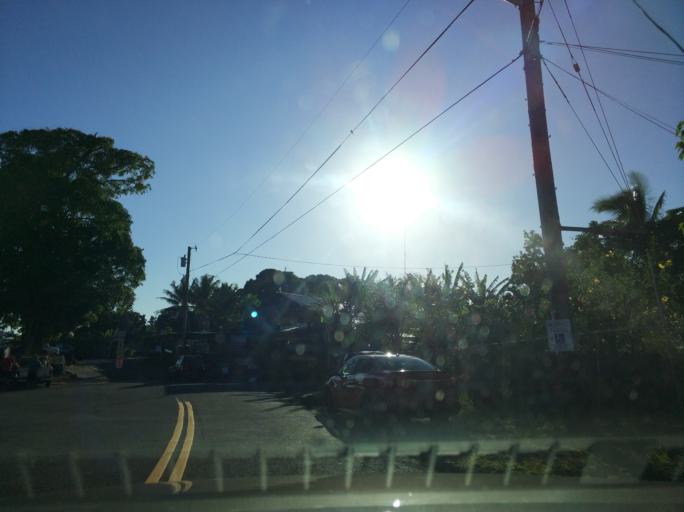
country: US
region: Hawaii
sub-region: Hawaii County
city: Leilani Estates
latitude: 19.3613
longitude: -154.9703
